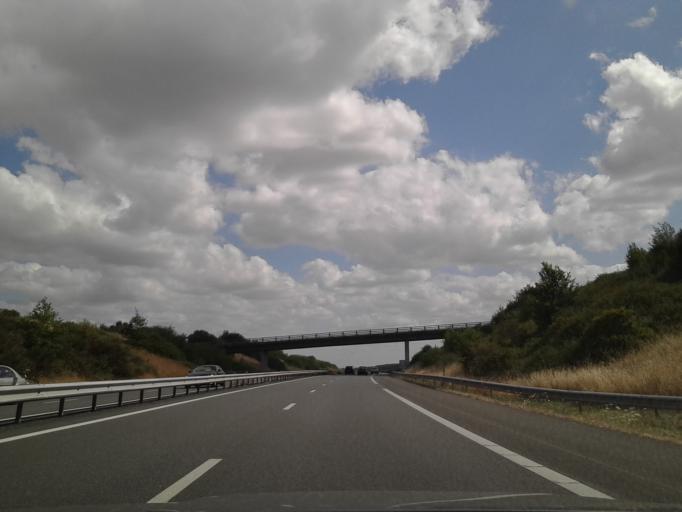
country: FR
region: Centre
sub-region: Departement du Cher
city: Orval
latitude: 46.6996
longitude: 2.4626
